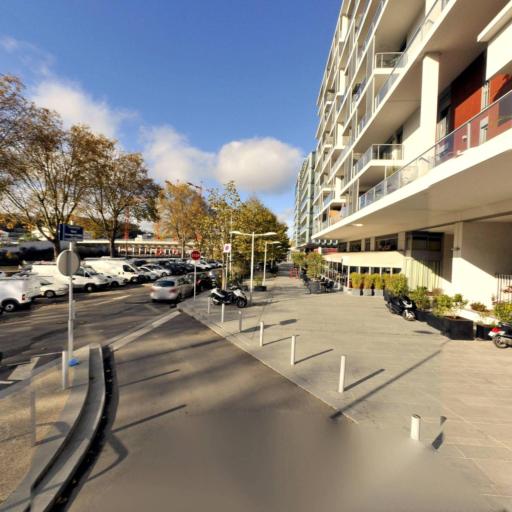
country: FR
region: Ile-de-France
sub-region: Departement des Hauts-de-Seine
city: Meudon
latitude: 48.8255
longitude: 2.2346
